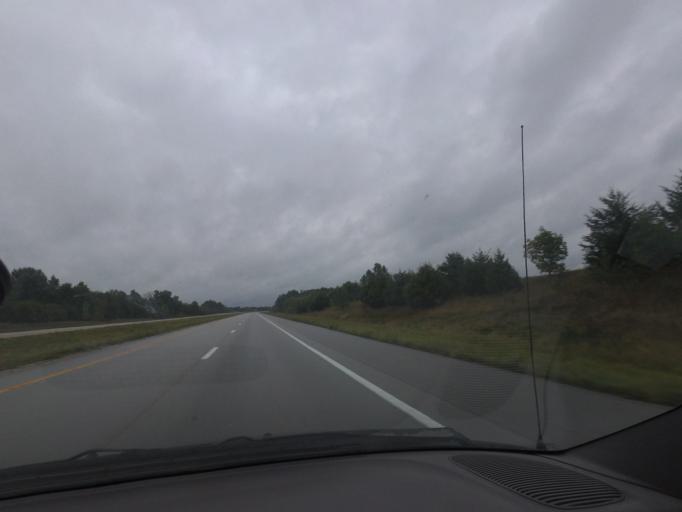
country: US
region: Missouri
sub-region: Marion County
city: Monroe City
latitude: 39.6609
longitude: -91.7457
